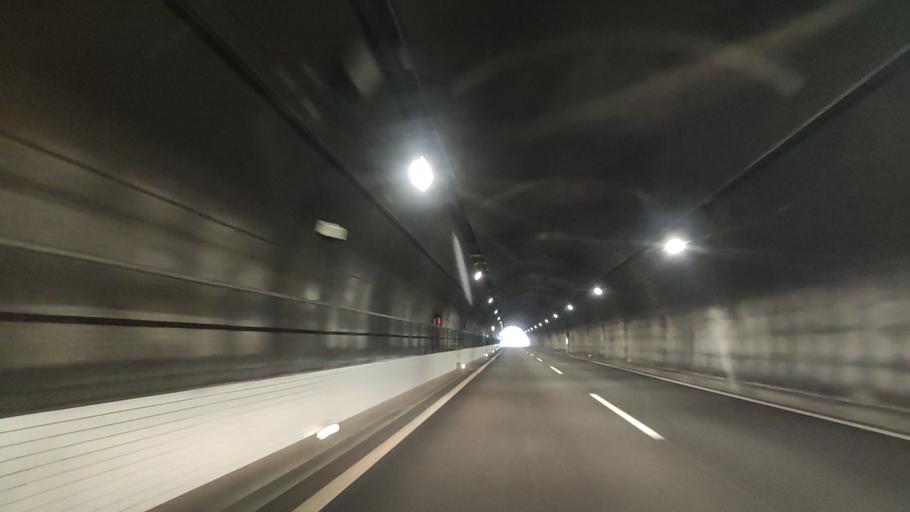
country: JP
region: Ehime
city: Saijo
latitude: 33.8485
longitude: 132.9960
